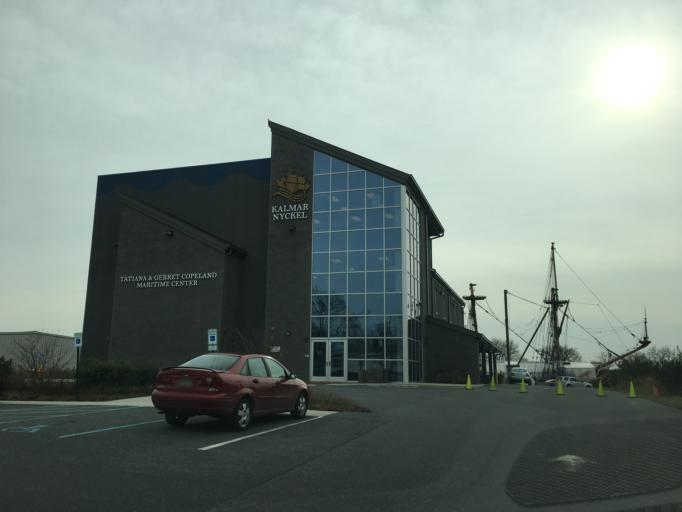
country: US
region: Delaware
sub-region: New Castle County
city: Wilmington
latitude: 39.7376
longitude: -75.5367
